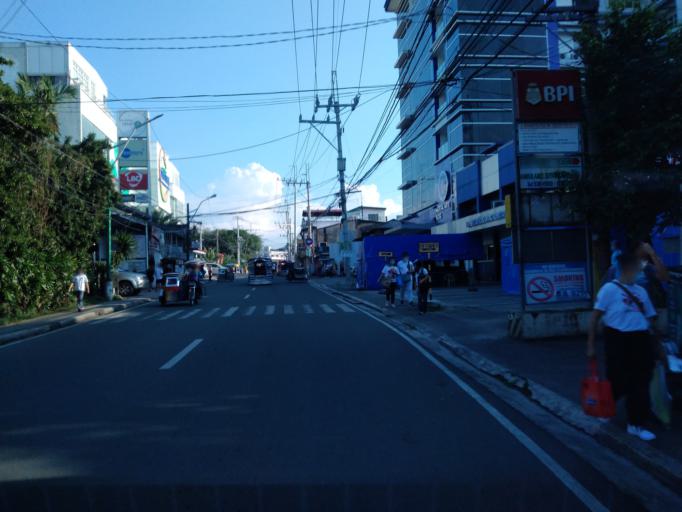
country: PH
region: Calabarzon
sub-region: Province of Laguna
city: Los Banos
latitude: 14.1712
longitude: 121.2434
